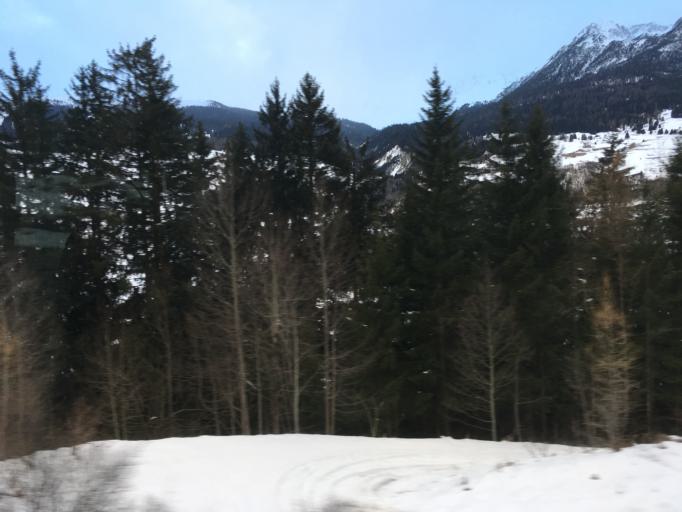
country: CH
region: Grisons
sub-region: Albula District
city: Tiefencastel
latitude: 46.6183
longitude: 9.5920
